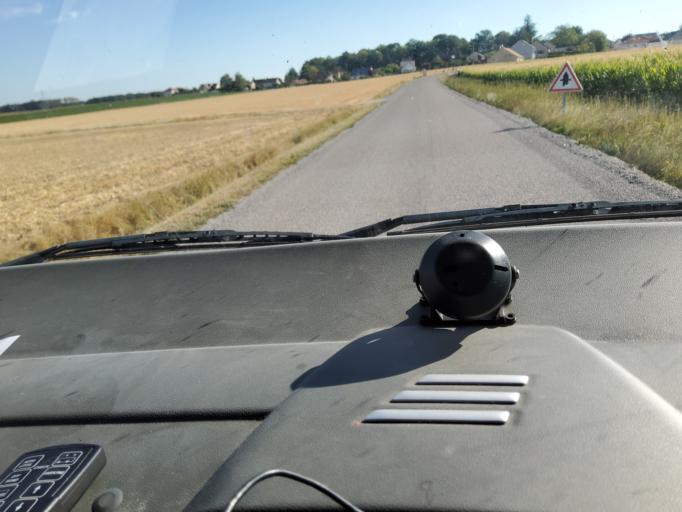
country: FR
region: Bourgogne
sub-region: Departement de la Cote-d'Or
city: Brazey-en-Plaine
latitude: 47.1391
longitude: 5.2384
